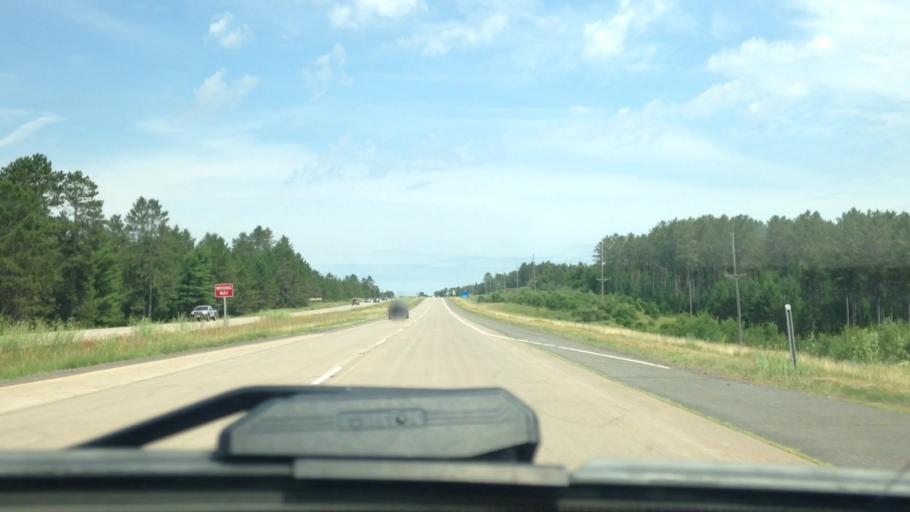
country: US
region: Wisconsin
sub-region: Douglas County
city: Lake Nebagamon
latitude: 46.3098
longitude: -91.8118
